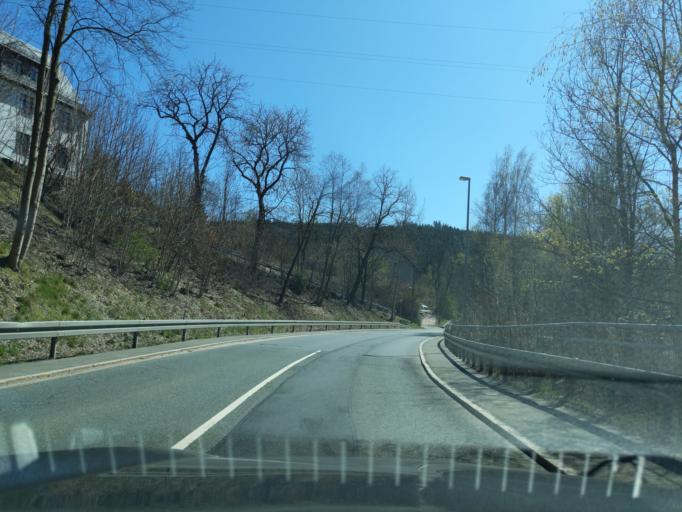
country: DE
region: Saxony
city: Stutzengrun
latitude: 50.5073
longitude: 12.5562
